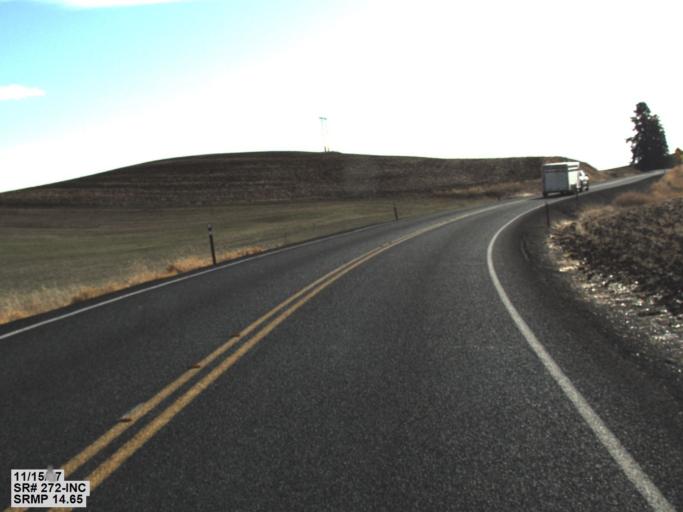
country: US
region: Washington
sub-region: Whitman County
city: Pullman
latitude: 46.9203
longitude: -117.1031
